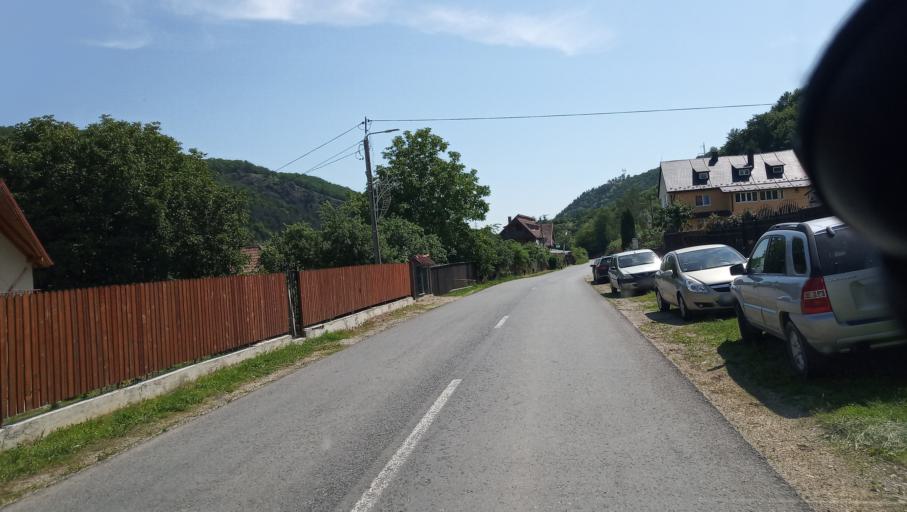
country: RO
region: Cluj
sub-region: Comuna Gilau
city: Gilau
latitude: 46.7314
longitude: 23.3355
